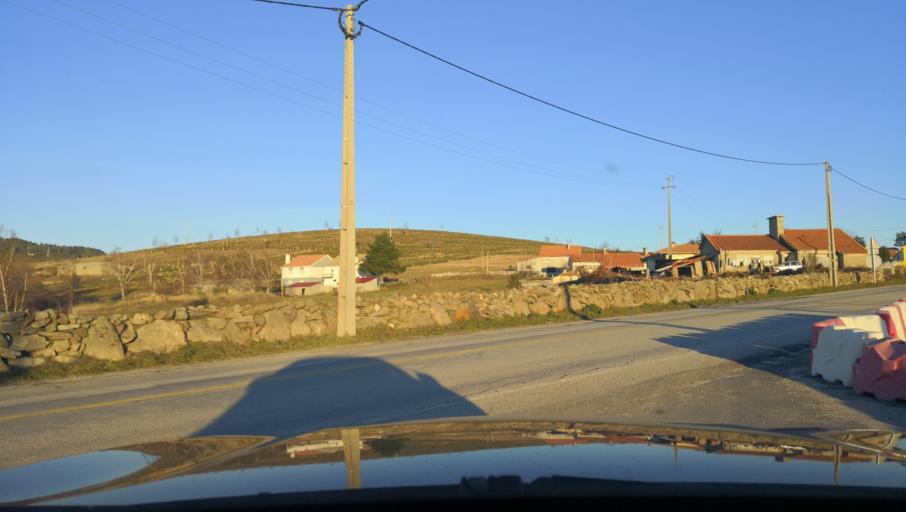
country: PT
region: Vila Real
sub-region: Ribeira de Pena
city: Ribeira de Pena
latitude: 41.4958
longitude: -7.7268
